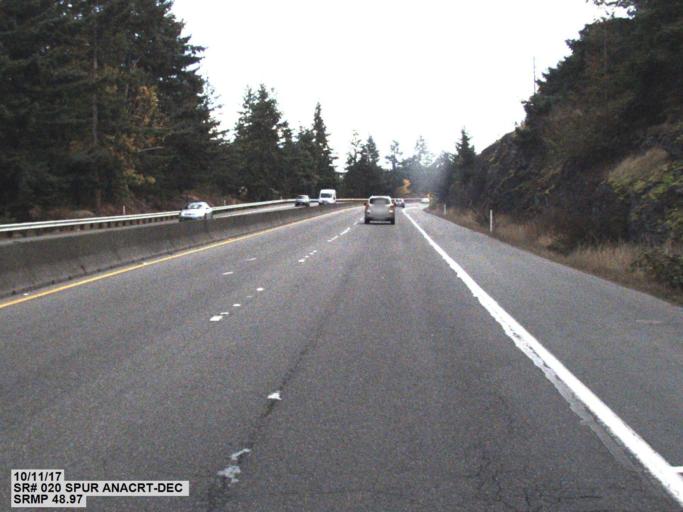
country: US
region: Washington
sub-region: Jefferson County
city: Port Hadlock-Irondale
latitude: 47.9903
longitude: -122.8668
